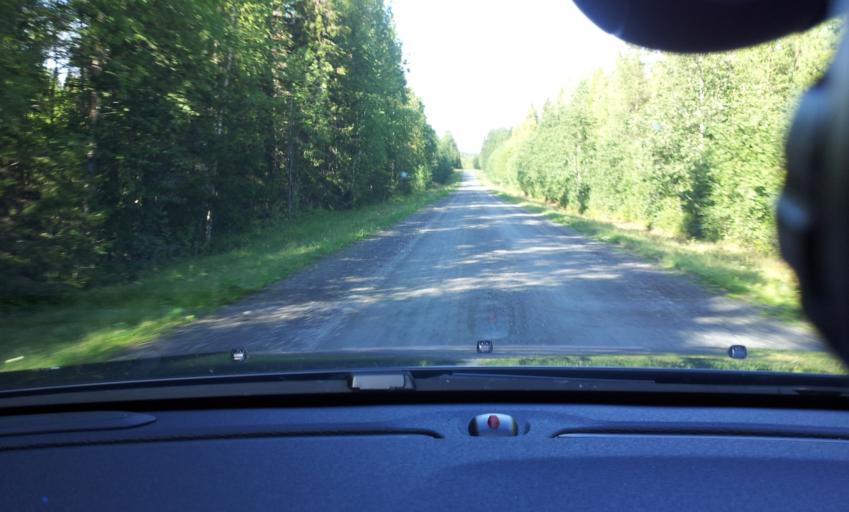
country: SE
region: Jaemtland
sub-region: Krokoms Kommun
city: Valla
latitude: 63.2662
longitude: 13.7834
